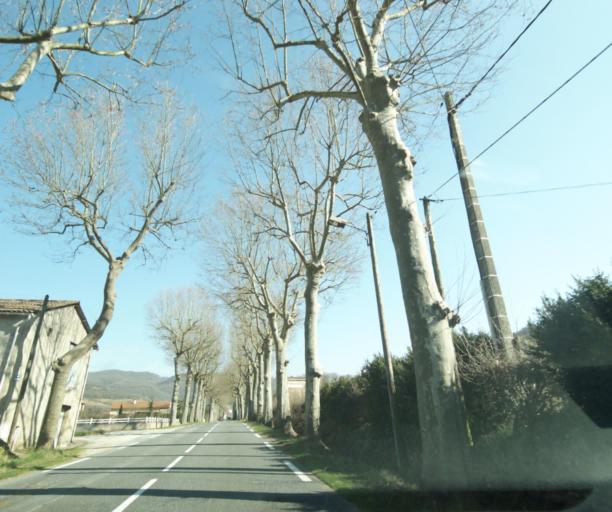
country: FR
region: Midi-Pyrenees
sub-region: Departement de l'Aveyron
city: Saint-Affrique
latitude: 43.9490
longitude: 2.8412
